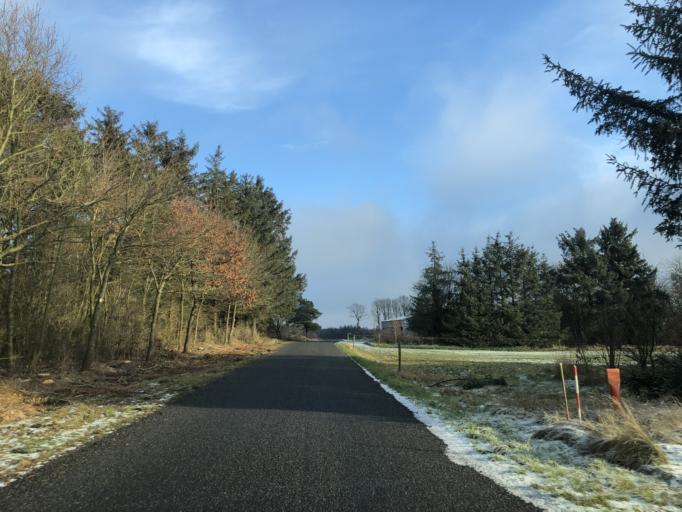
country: DK
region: Central Jutland
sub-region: Holstebro Kommune
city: Ulfborg
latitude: 56.2067
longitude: 8.3623
